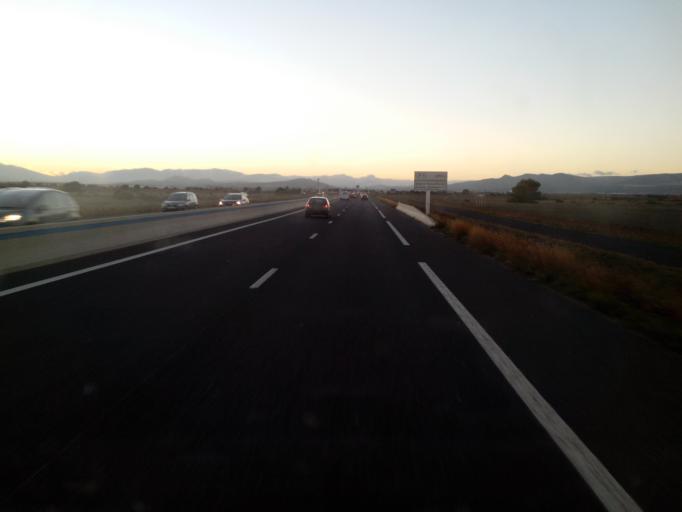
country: FR
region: Languedoc-Roussillon
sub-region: Departement des Pyrenees-Orientales
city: Claira
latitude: 42.7775
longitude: 2.9357
